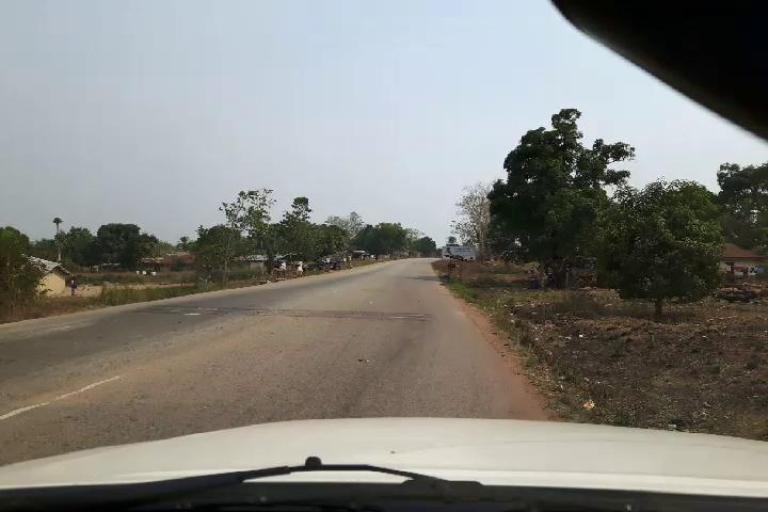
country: SL
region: Southern Province
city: Largo
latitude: 8.3199
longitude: -12.2162
